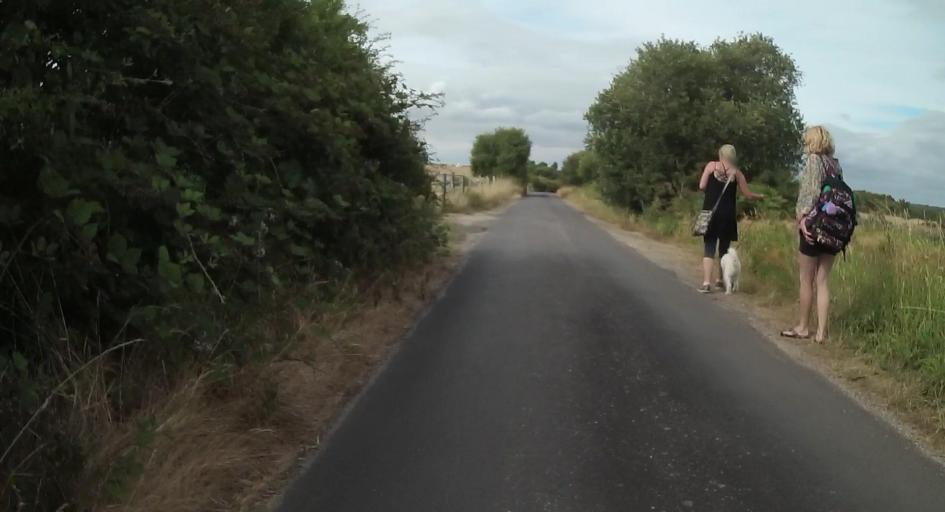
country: GB
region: England
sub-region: Dorset
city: Wareham
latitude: 50.6649
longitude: -2.0855
